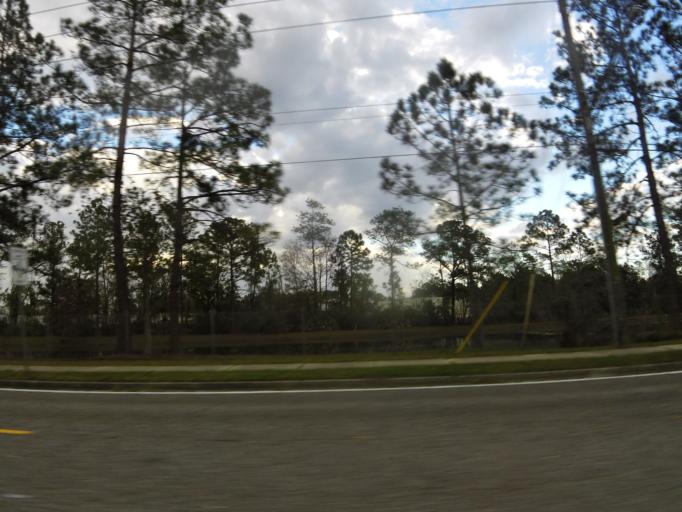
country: US
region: Florida
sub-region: Saint Johns County
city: Fruit Cove
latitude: 30.2133
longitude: -81.5849
